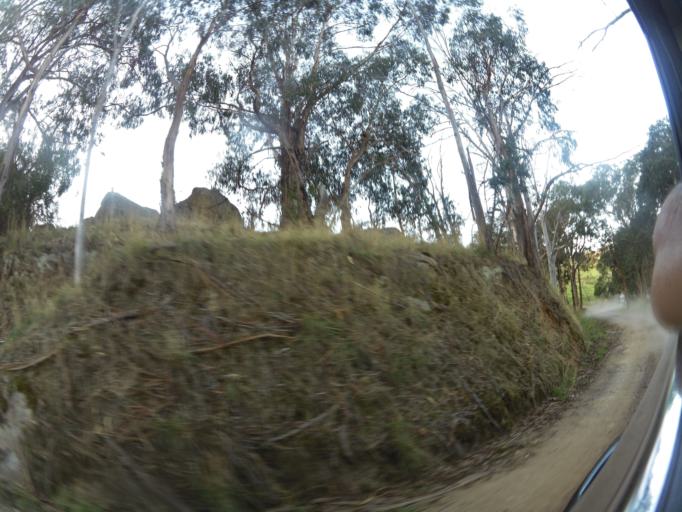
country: AU
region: Victoria
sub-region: Murrindindi
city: Alexandra
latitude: -37.1448
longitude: 145.5184
